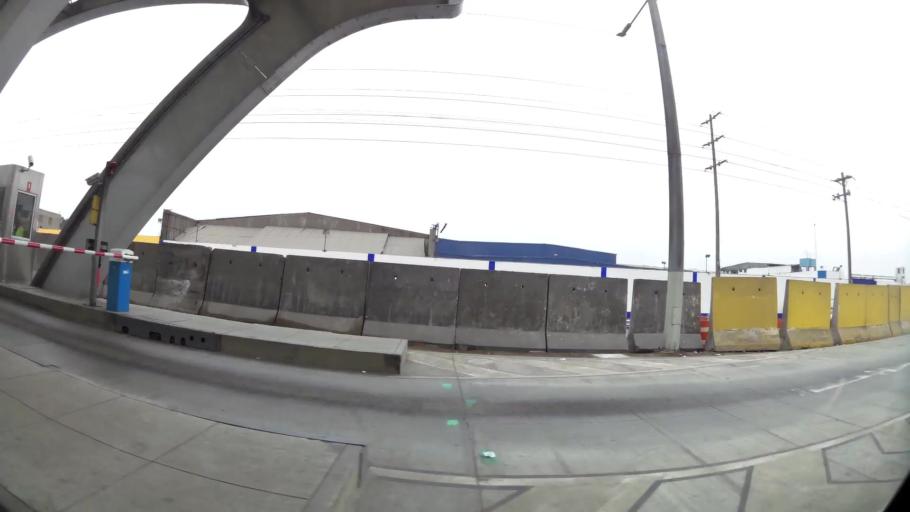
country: PE
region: Lima
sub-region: Lima
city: Urb. Santo Domingo
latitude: -11.9104
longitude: -77.0716
